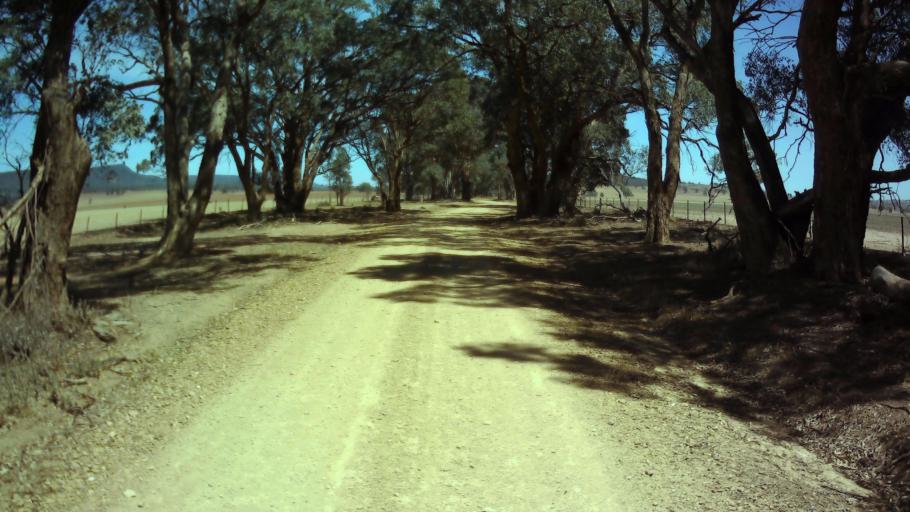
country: AU
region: New South Wales
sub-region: Weddin
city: Grenfell
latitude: -33.9685
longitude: 148.1374
